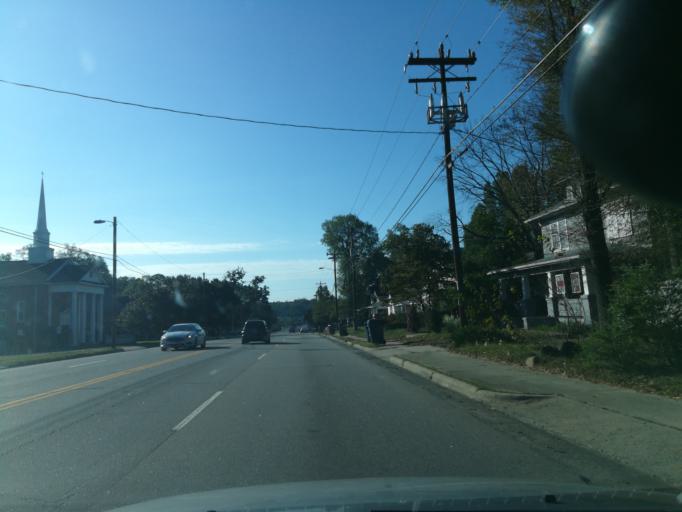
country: US
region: North Carolina
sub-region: Durham County
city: Durham
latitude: 36.0226
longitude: -78.8900
